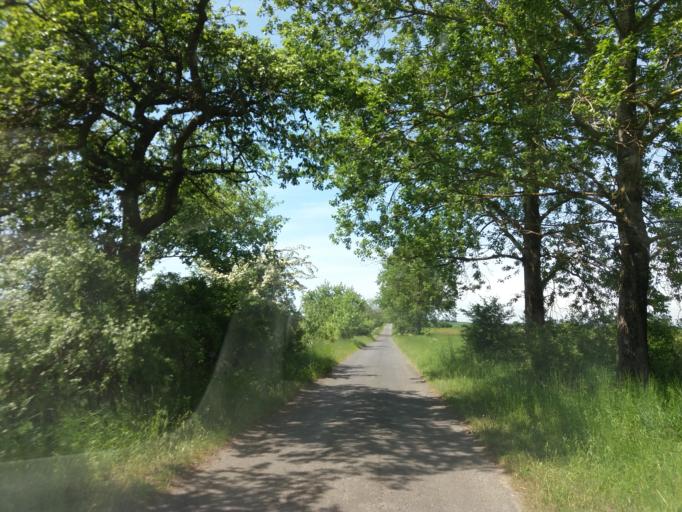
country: PL
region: West Pomeranian Voivodeship
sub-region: Powiat stargardzki
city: Dobrzany
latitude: 53.3506
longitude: 15.4510
